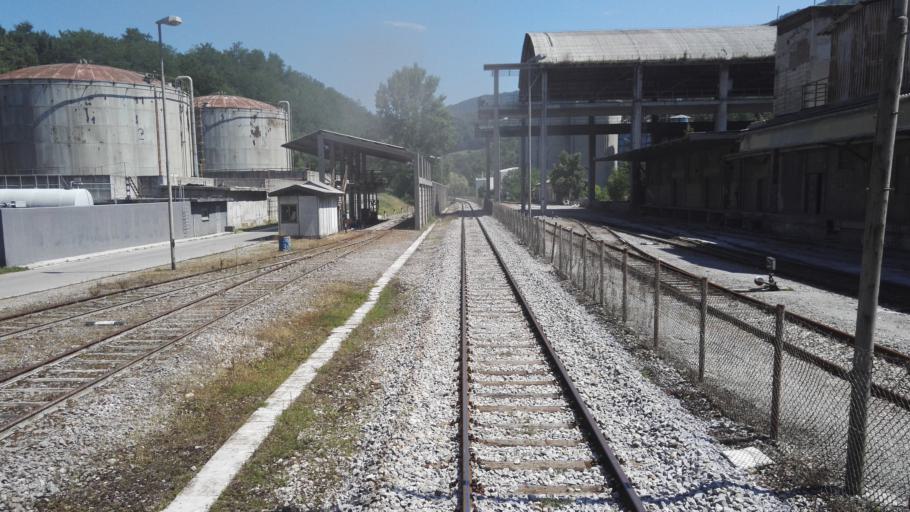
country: SI
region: Kanal
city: Deskle
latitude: 46.0621
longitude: 13.6248
